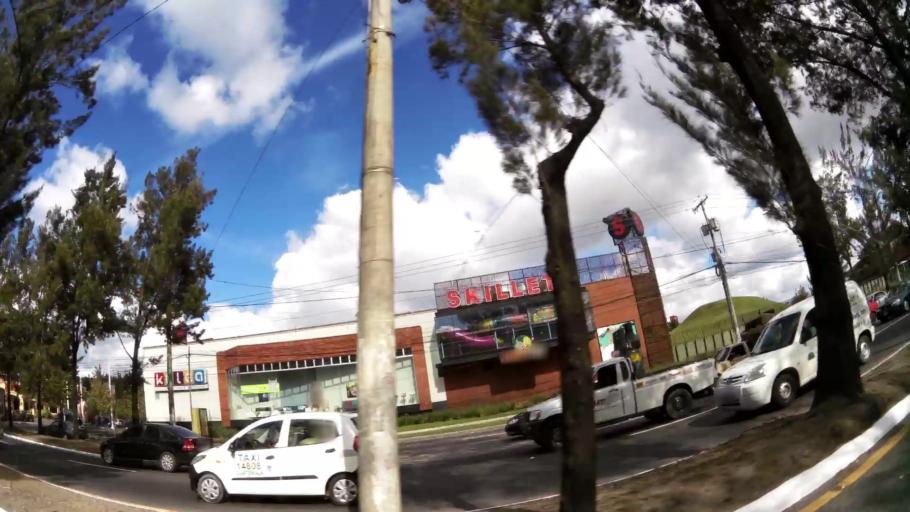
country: GT
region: Guatemala
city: Guatemala City
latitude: 14.6201
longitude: -90.5568
